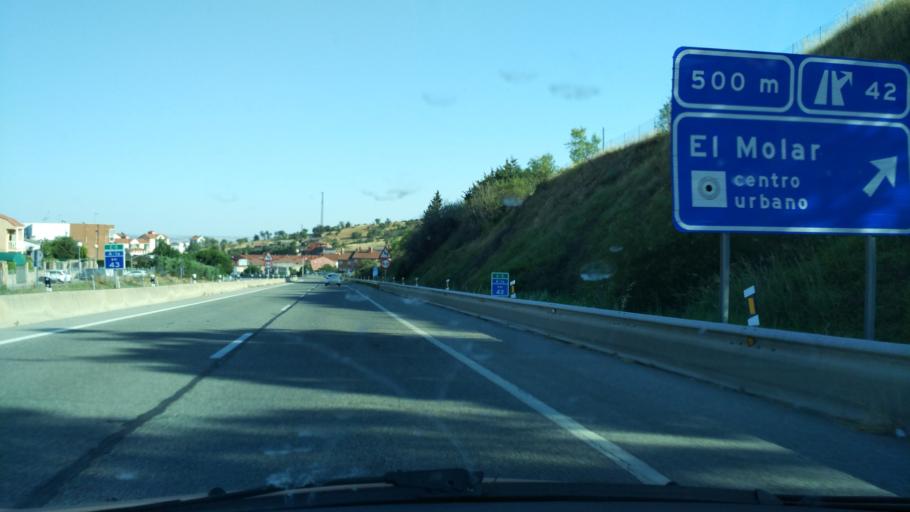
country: ES
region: Madrid
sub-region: Provincia de Madrid
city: El Molar
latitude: 40.7357
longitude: -3.5864
